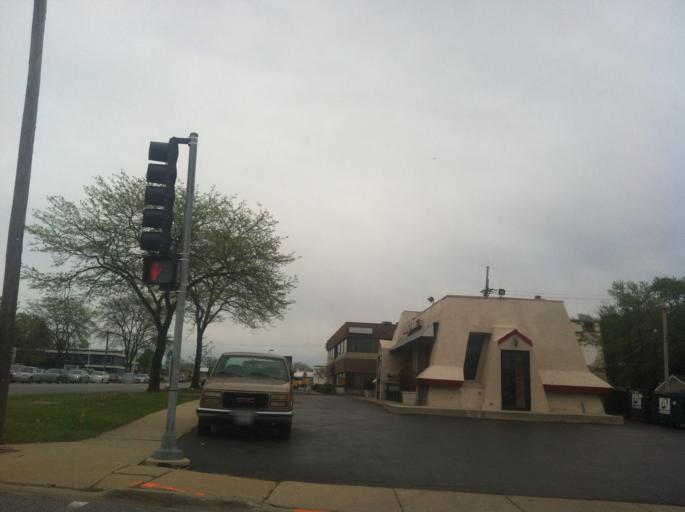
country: US
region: Illinois
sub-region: DuPage County
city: Downers Grove
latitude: 41.8087
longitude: -88.0108
